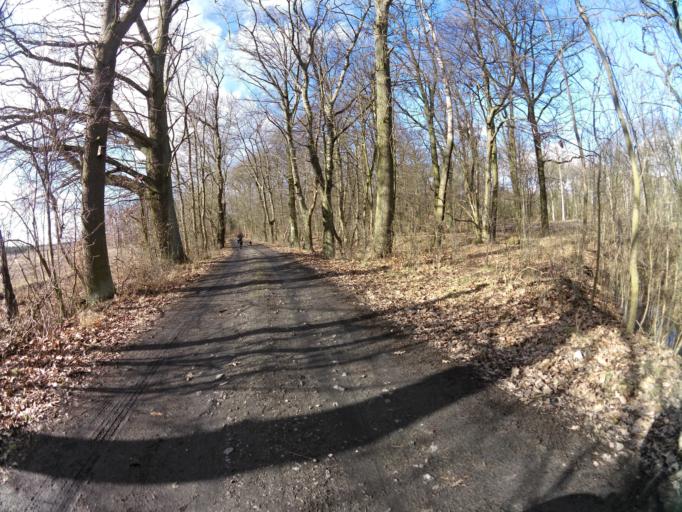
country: PL
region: West Pomeranian Voivodeship
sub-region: Powiat mysliborski
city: Debno
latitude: 52.7609
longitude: 14.7171
